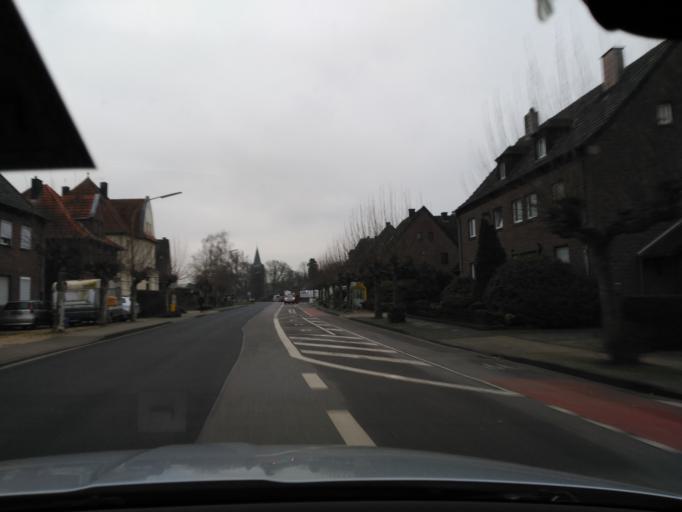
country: DE
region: North Rhine-Westphalia
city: Wegberg
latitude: 51.1349
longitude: 6.3012
